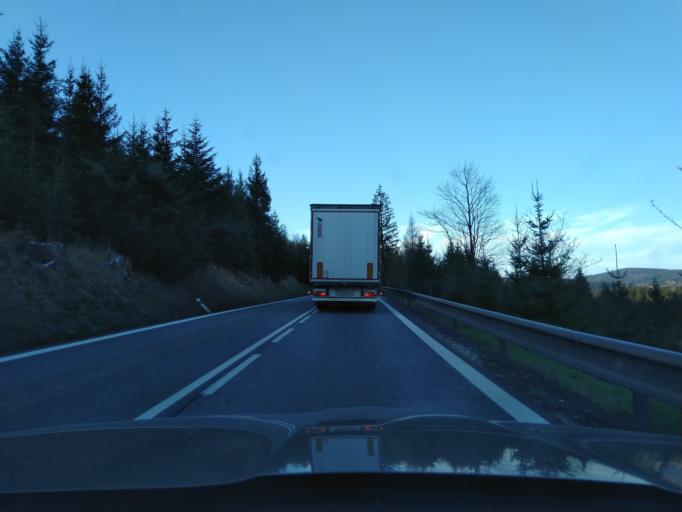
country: CZ
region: Jihocesky
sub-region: Okres Prachatice
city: Vimperk
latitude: 49.0449
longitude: 13.7611
